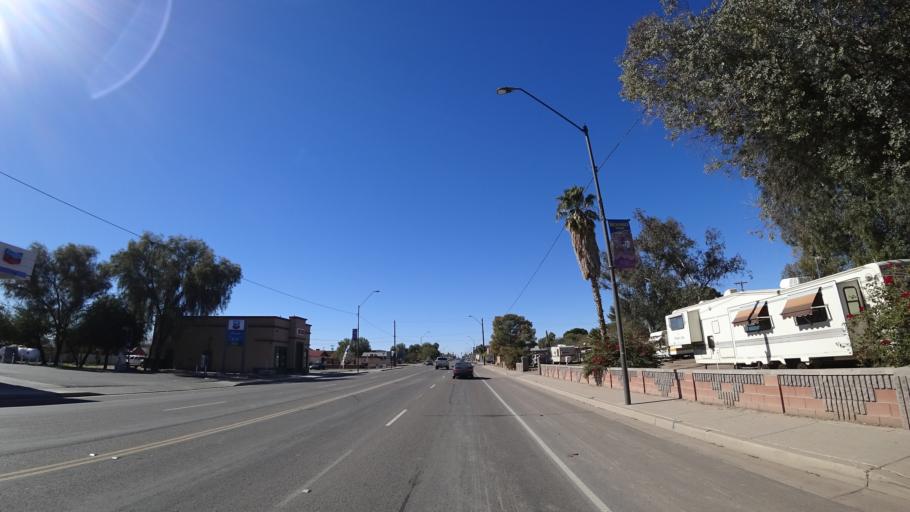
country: US
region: Arizona
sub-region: Maricopa County
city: Buckeye
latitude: 33.3706
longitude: -112.5788
